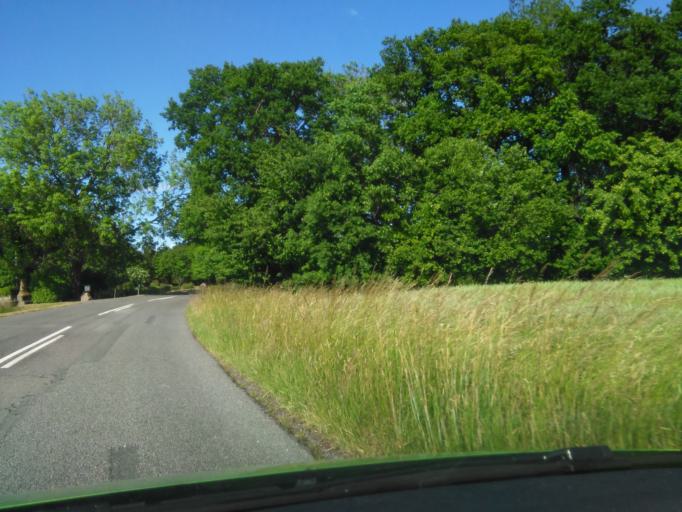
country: DK
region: Capital Region
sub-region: Bornholm Kommune
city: Nexo
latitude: 55.0637
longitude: 15.0774
